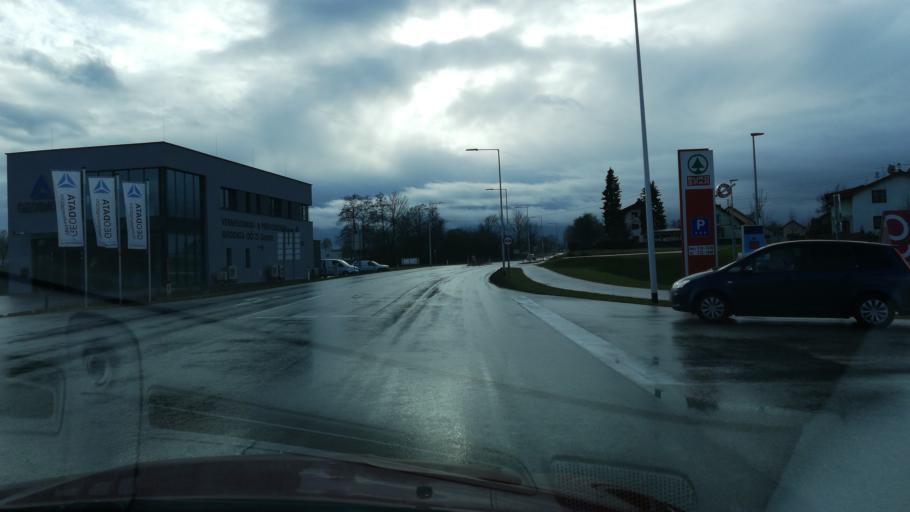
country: AT
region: Upper Austria
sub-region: Wels-Land
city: Sattledt
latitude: 48.0699
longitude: 14.0542
